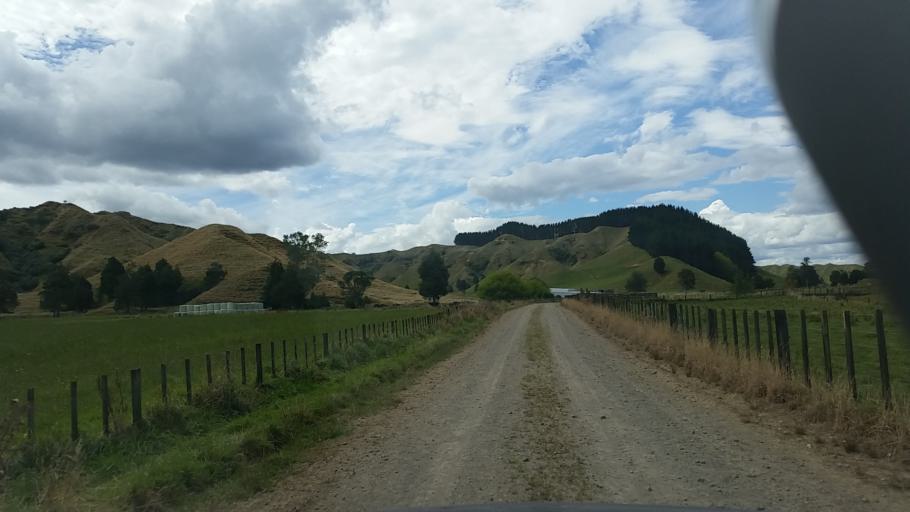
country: NZ
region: Taranaki
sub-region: South Taranaki District
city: Eltham
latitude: -39.2841
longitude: 174.4966
